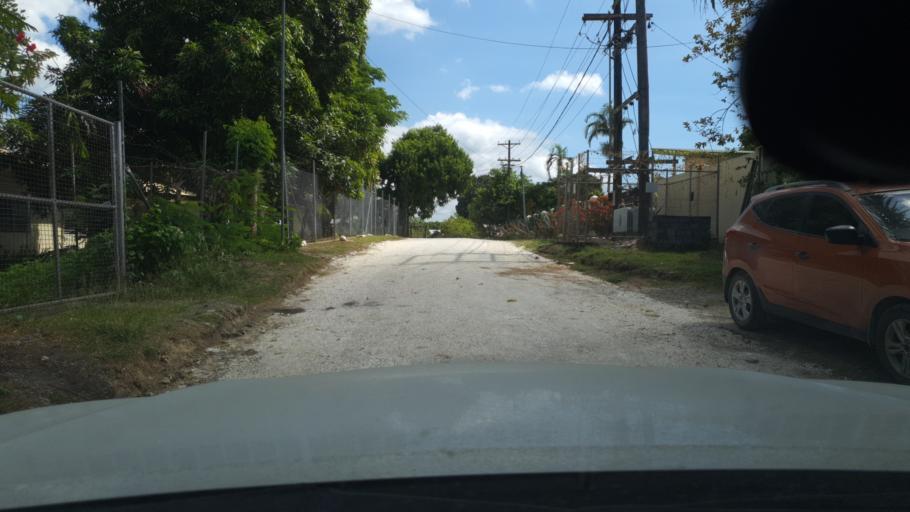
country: SB
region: Guadalcanal
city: Honiara
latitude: -9.4303
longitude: 159.9380
